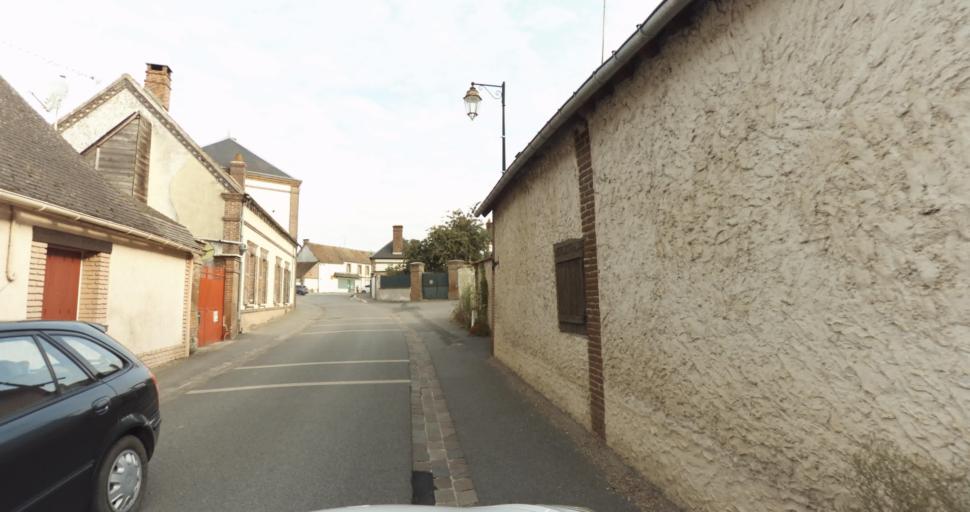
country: FR
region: Haute-Normandie
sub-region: Departement de l'Eure
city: Saint-Germain-sur-Avre
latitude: 48.8193
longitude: 1.2673
